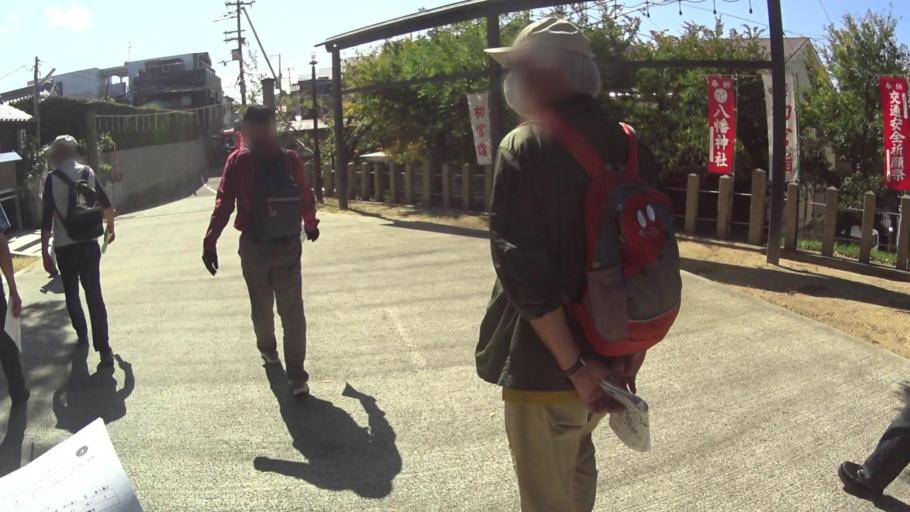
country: JP
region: Osaka
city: Takaishi
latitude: 34.5362
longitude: 135.4751
